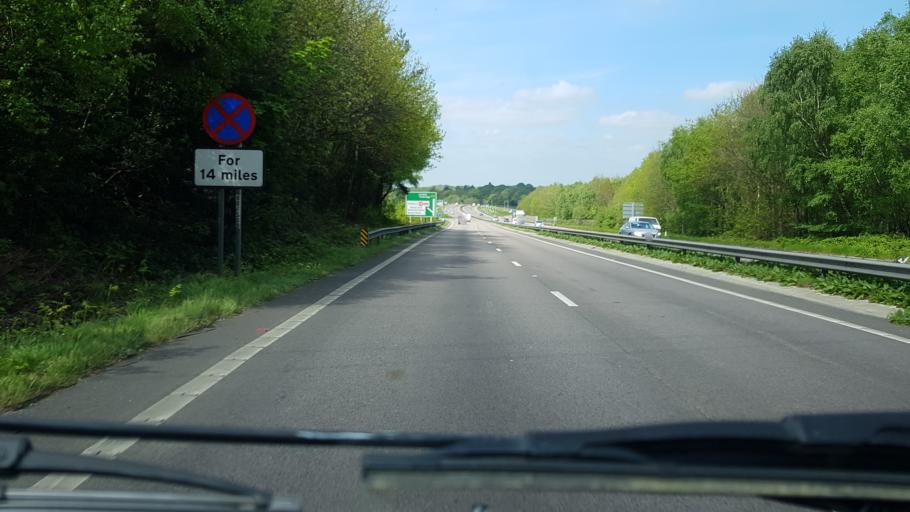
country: GB
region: England
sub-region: Kent
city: Pembury
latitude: 51.1505
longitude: 0.3028
